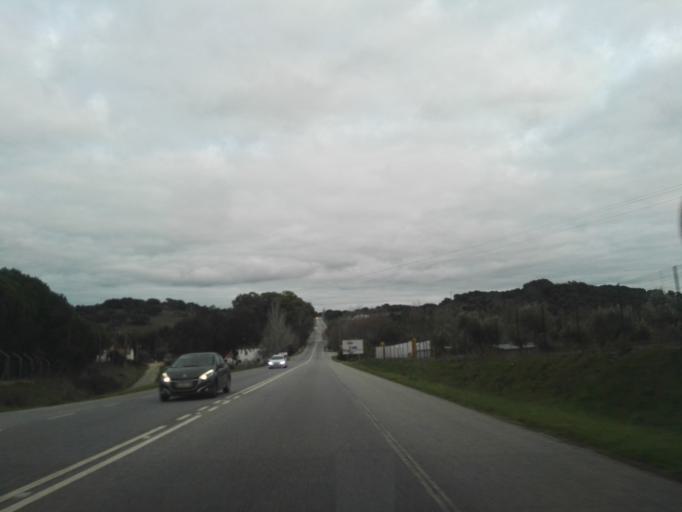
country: PT
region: Evora
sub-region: Montemor-O-Novo
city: Montemor-o-Novo
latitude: 38.6448
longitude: -8.1948
